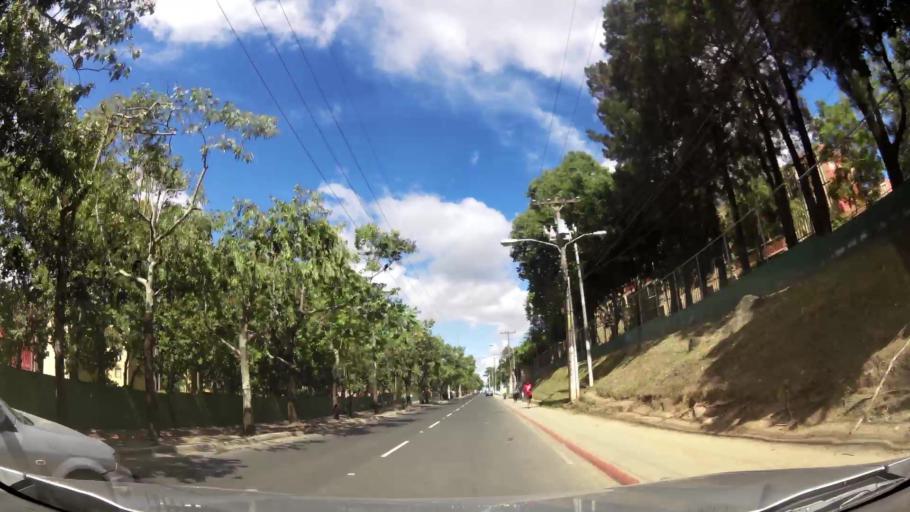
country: GT
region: Guatemala
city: Villa Nueva
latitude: 14.5473
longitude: -90.5522
